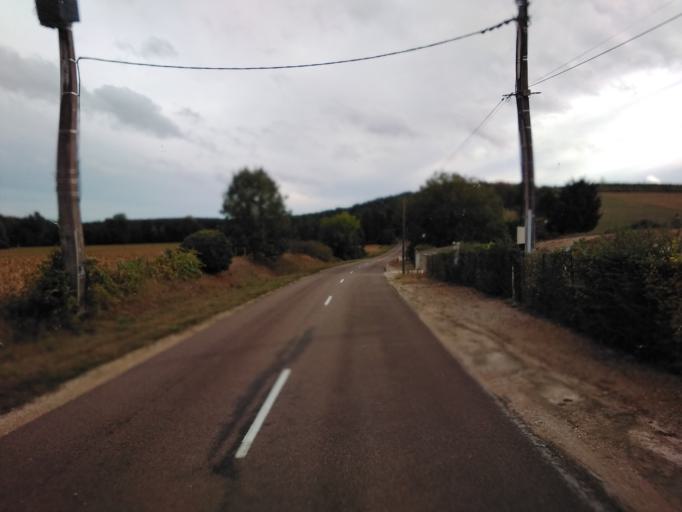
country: FR
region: Champagne-Ardenne
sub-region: Departement de l'Aube
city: Les Riceys
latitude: 47.9756
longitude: 4.3564
